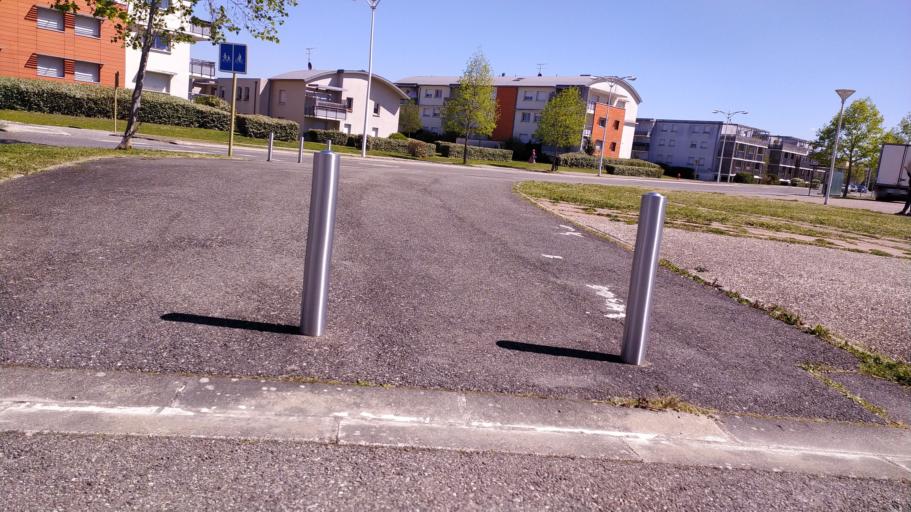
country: FR
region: Midi-Pyrenees
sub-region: Departement de la Haute-Garonne
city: Tournefeuille
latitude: 43.5768
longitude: 1.3136
